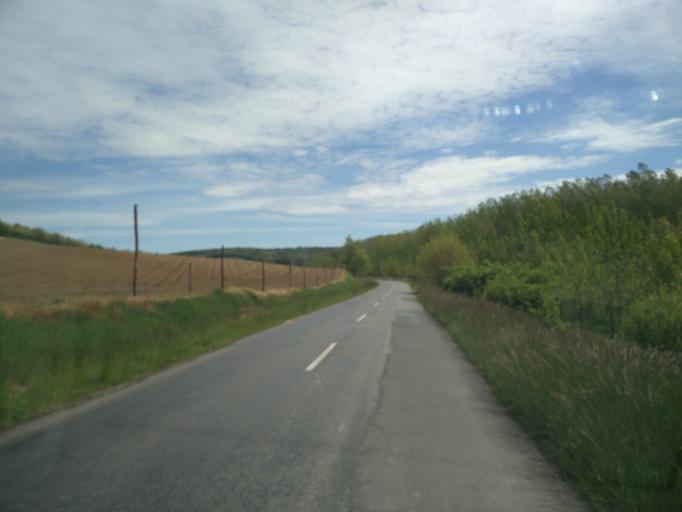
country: HU
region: Tolna
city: Szekszard
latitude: 46.2839
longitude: 18.6504
